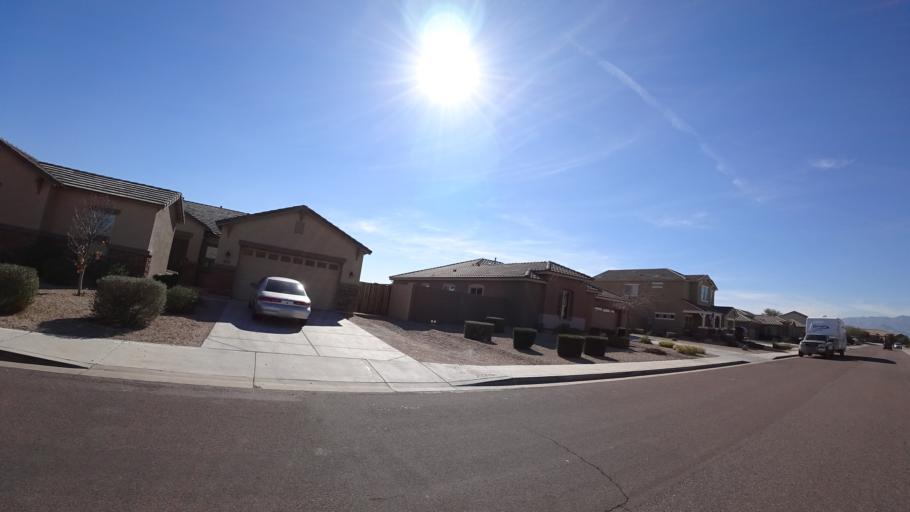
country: US
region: Arizona
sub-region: Maricopa County
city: Citrus Park
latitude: 33.5122
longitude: -112.4584
